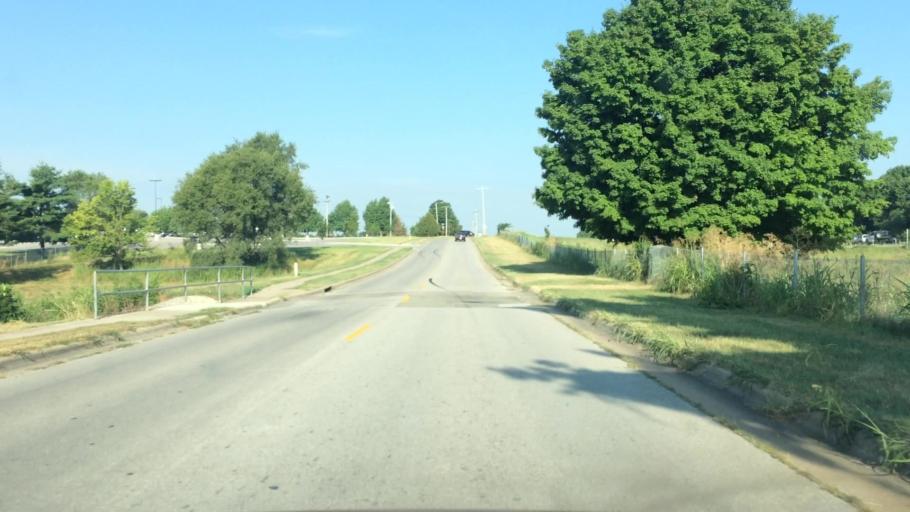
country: US
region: Missouri
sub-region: Greene County
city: Springfield
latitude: 37.2498
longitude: -93.2672
